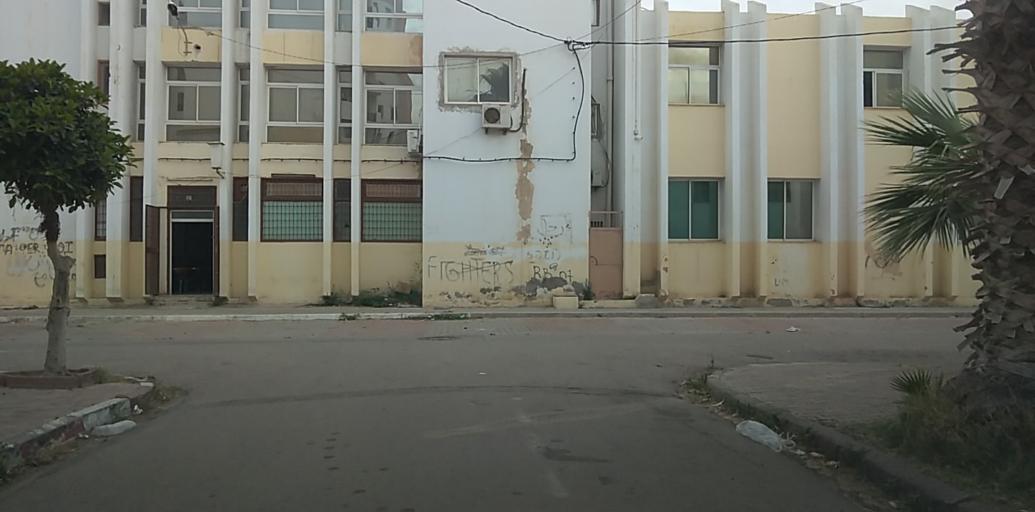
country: TN
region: Safaqis
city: Sfax
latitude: 34.7318
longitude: 10.7666
